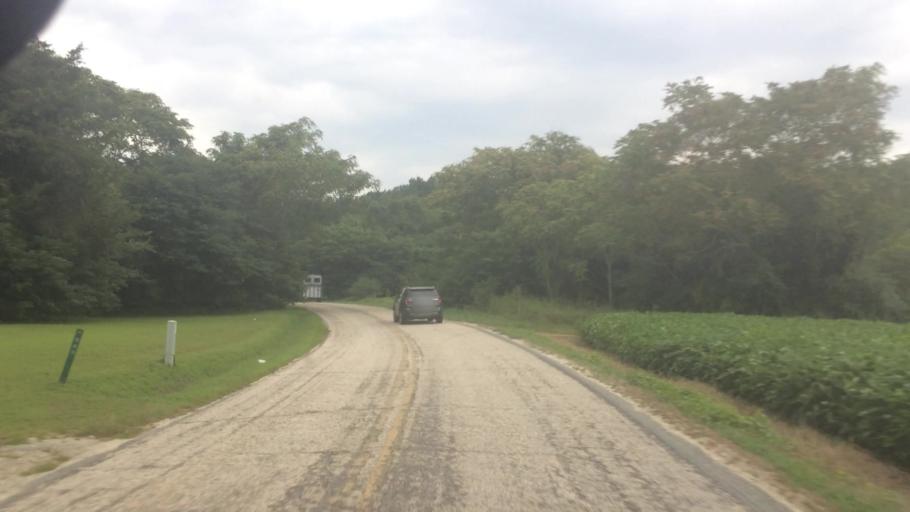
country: US
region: Virginia
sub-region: King William County
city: West Point
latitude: 37.5532
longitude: -76.7284
